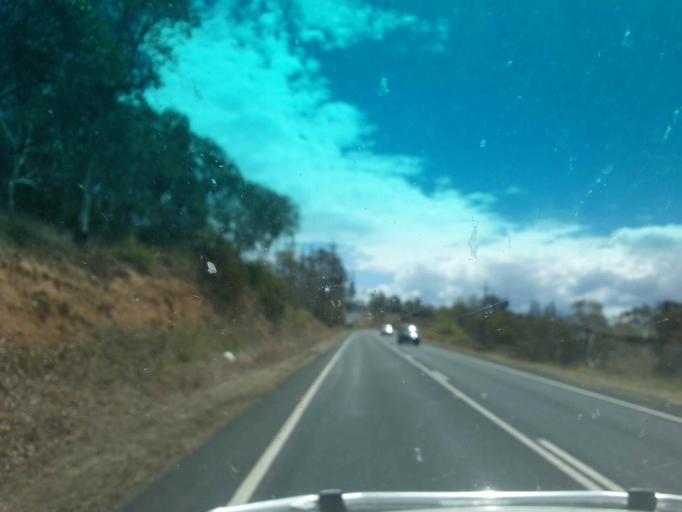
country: AU
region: New South Wales
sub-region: Snowy River
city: Jindabyne
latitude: -36.4271
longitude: 148.6216
